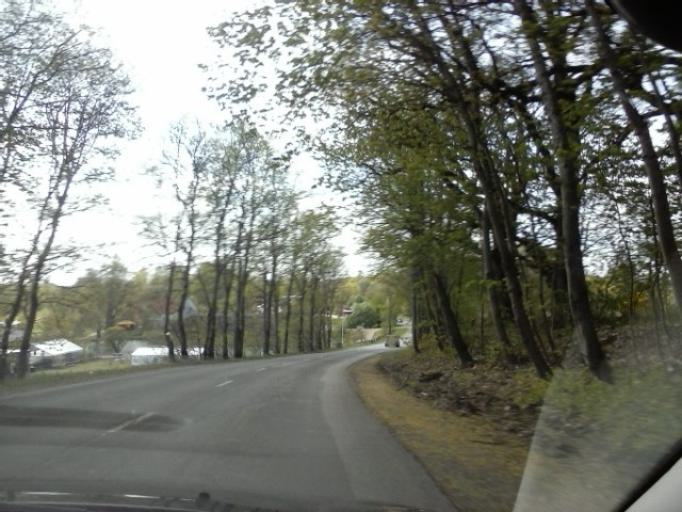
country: LV
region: Sigulda
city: Sigulda
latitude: 57.1905
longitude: 24.8469
